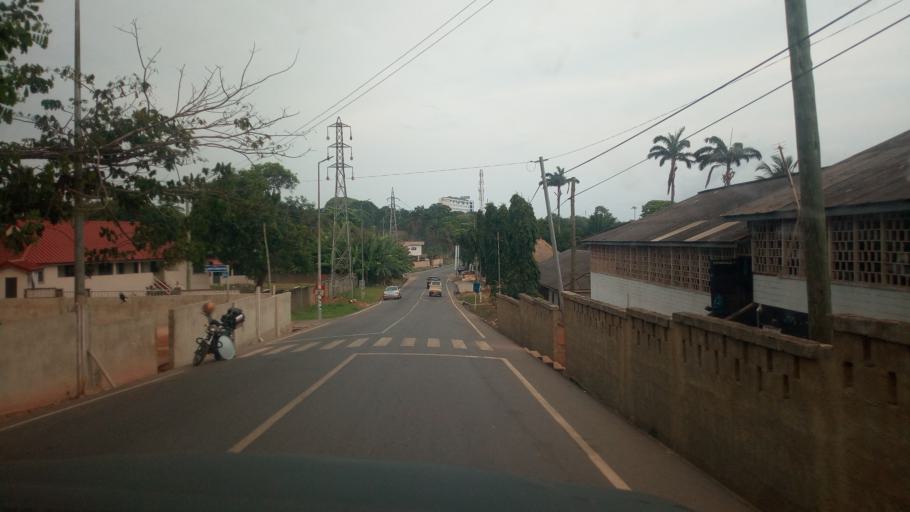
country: GH
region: Western
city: Takoradi
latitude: 4.8798
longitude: -1.7605
